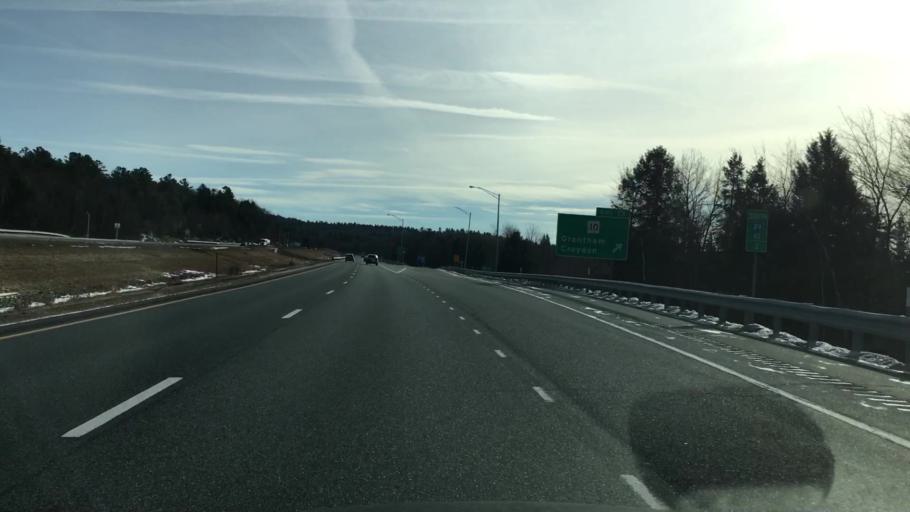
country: US
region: New Hampshire
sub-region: Sullivan County
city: Grantham
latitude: 43.5015
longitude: -72.1340
